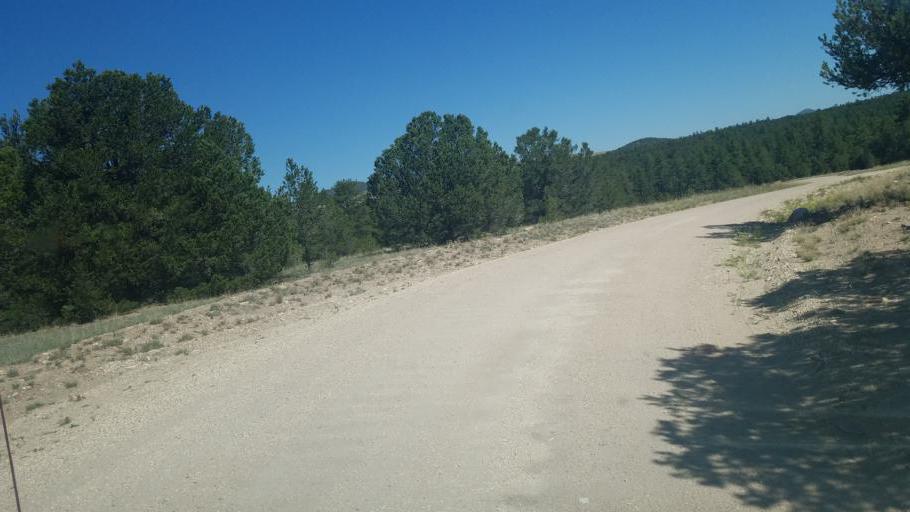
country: US
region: Colorado
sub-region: Custer County
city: Westcliffe
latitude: 38.2903
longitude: -105.4609
